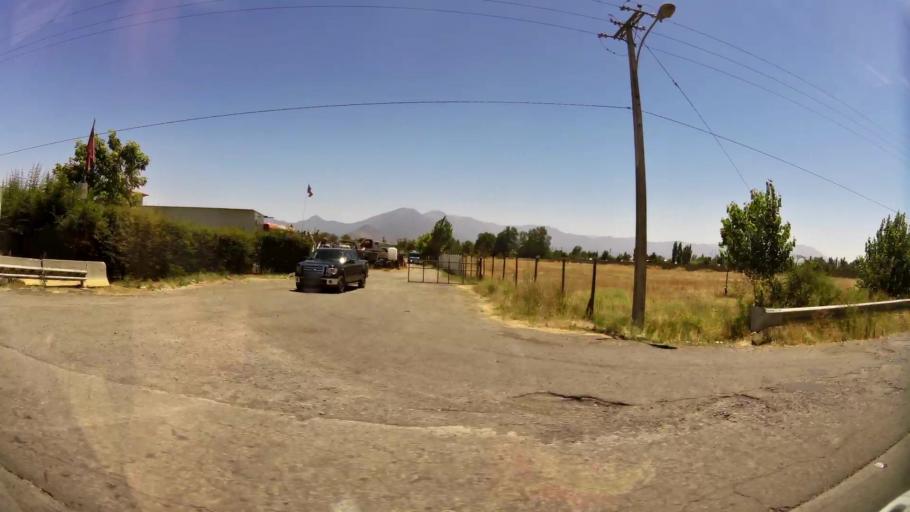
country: CL
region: O'Higgins
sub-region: Provincia de Cachapoal
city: Rancagua
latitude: -34.2229
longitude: -70.7790
